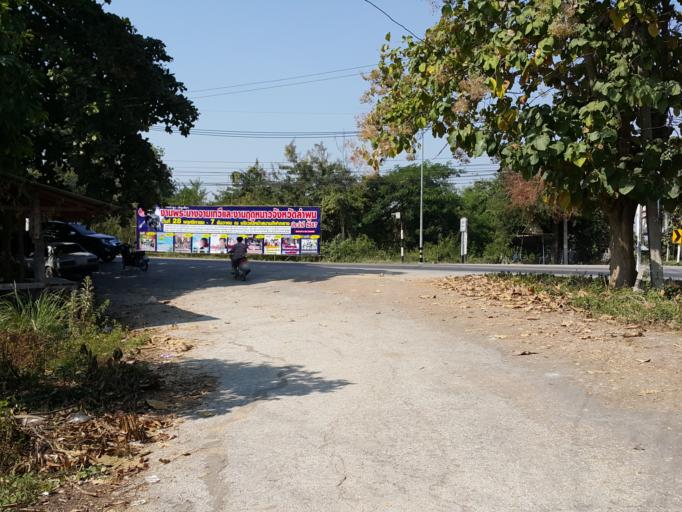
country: TH
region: Lamphun
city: Pa Sang
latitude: 18.5427
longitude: 98.9398
